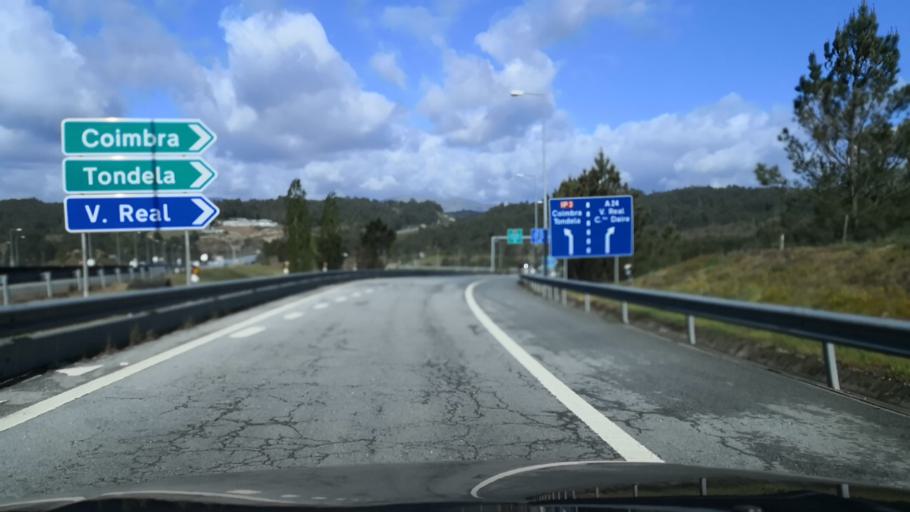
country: PT
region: Viseu
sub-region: Viseu
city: Viseu
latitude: 40.6251
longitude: -7.9566
